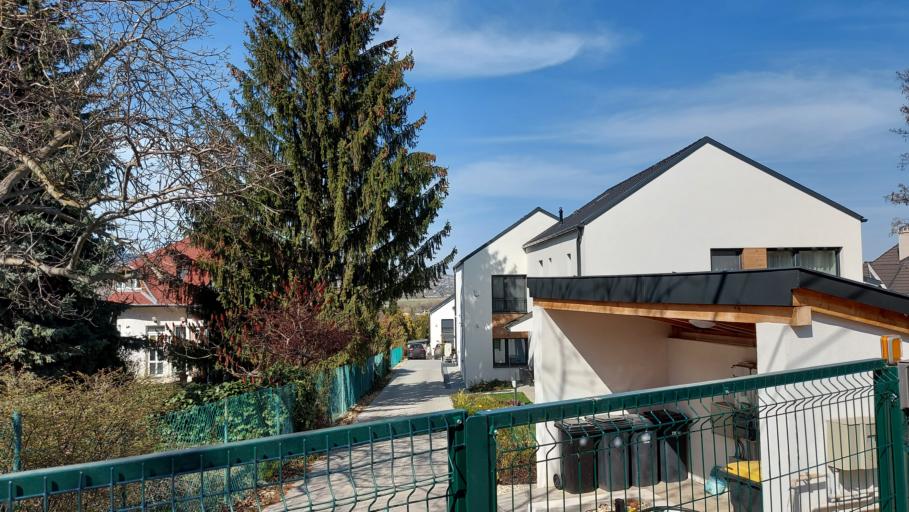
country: HU
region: Pest
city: Budaors
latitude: 47.4333
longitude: 18.9747
